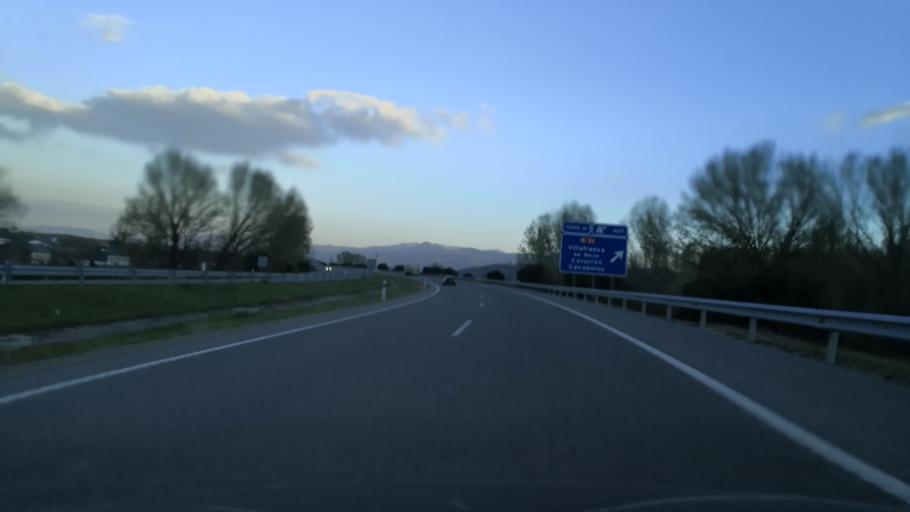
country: ES
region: Castille and Leon
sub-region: Provincia de Leon
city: Villafranca del Bierzo
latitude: 42.5992
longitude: -6.8148
